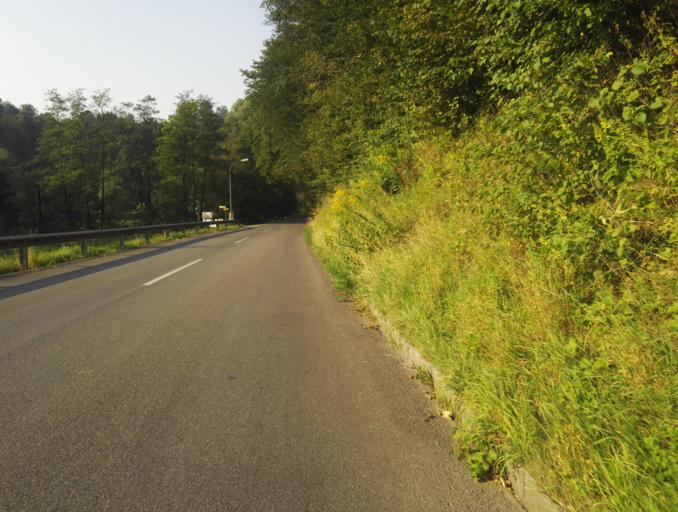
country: AT
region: Styria
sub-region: Politischer Bezirk Graz-Umgebung
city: Gratwein
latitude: 47.1211
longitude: 15.2982
